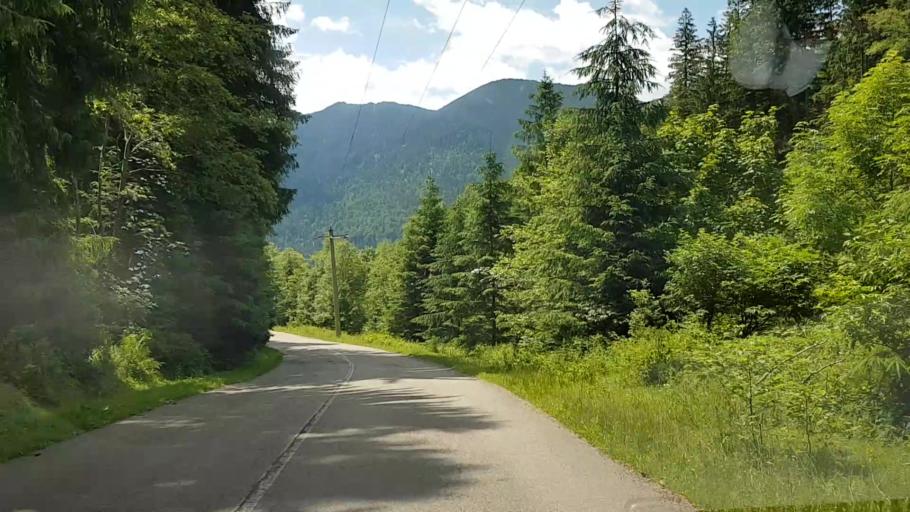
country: RO
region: Suceava
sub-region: Comuna Crucea
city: Crucea
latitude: 47.4083
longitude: 25.5777
